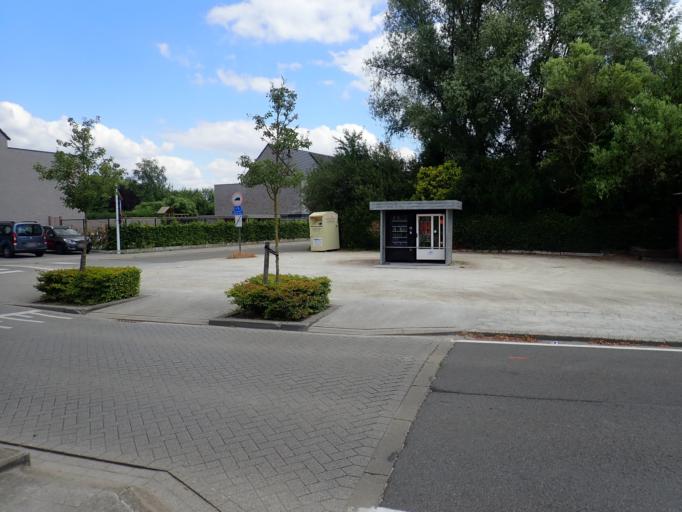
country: BE
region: Flanders
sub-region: Provincie Vlaams-Brabant
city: Tremelo
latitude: 51.0244
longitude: 4.6946
